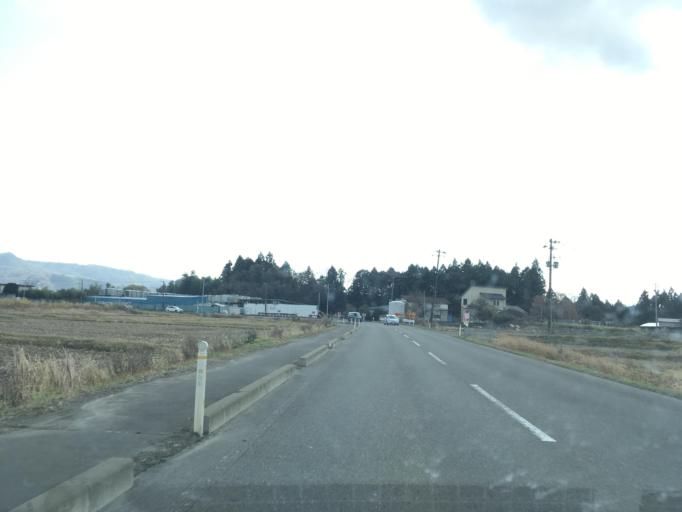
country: JP
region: Miyagi
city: Sendai
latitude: 38.2824
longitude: 140.7568
